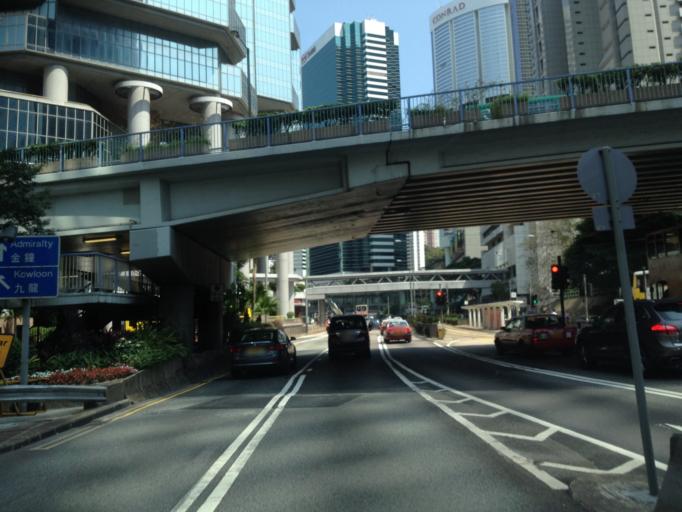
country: HK
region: Central and Western
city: Central
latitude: 22.2797
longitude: 114.1624
